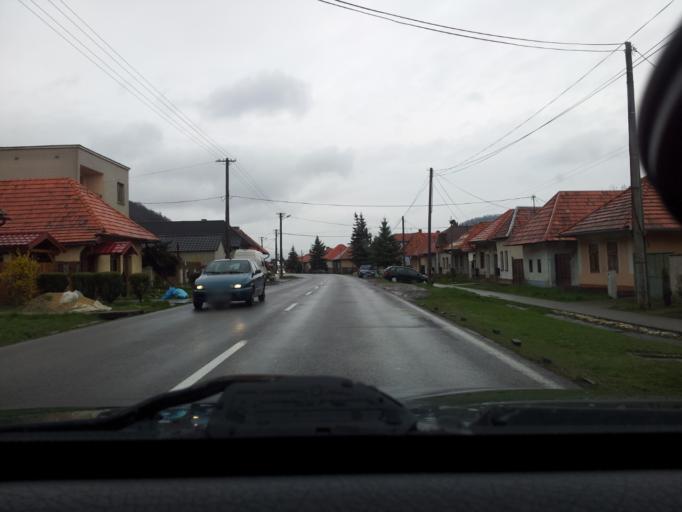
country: SK
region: Nitriansky
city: Tlmace
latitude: 48.3480
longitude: 18.5626
